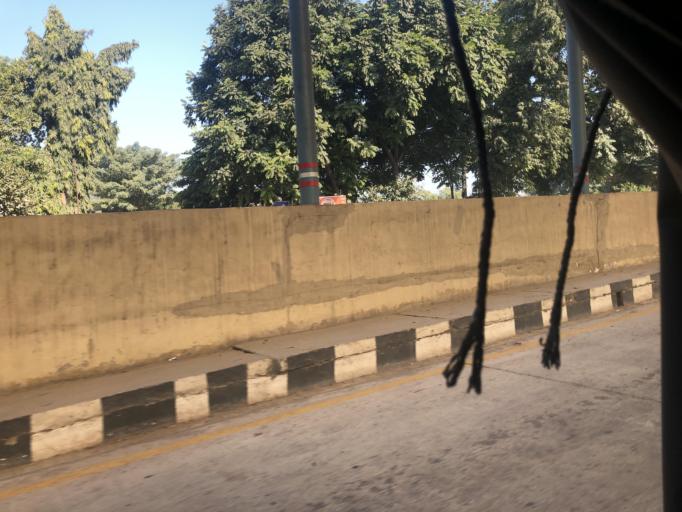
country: IN
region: Haryana
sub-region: Gurgaon
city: Gurgaon
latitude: 28.4664
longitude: 77.0610
